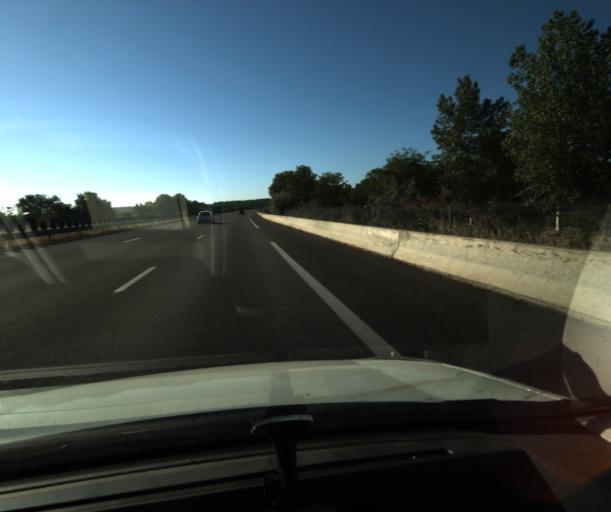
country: FR
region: Midi-Pyrenees
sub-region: Departement de la Haute-Garonne
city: Castelnau-d'Estretefonds
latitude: 43.8125
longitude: 1.3597
